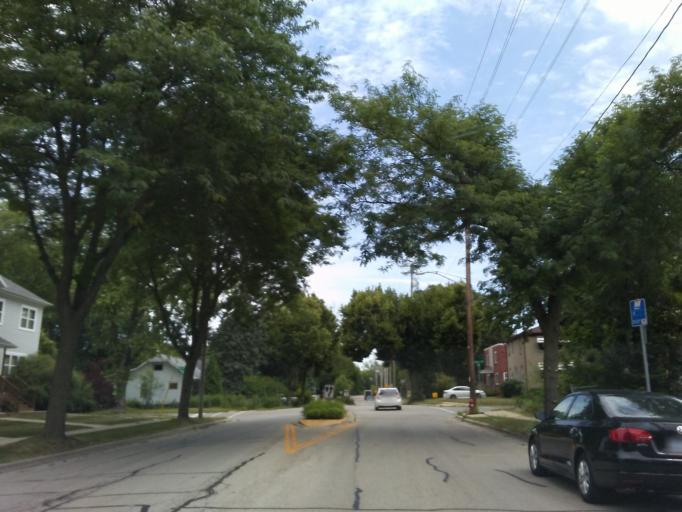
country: US
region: Wisconsin
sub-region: Dane County
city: Maple Bluff
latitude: 43.1067
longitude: -89.3435
